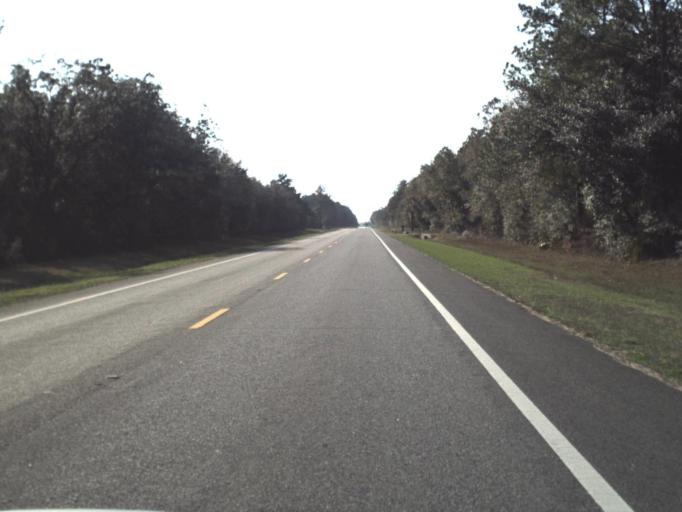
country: US
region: Florida
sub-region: Bay County
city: Youngstown
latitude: 30.4365
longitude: -85.4993
